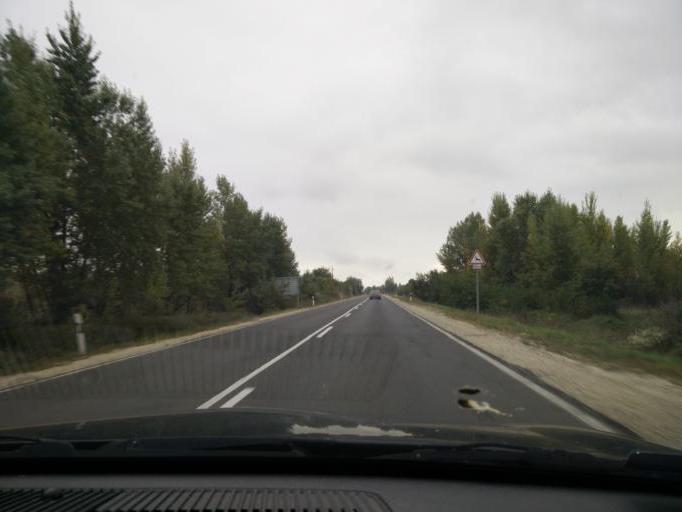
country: HU
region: Komarom-Esztergom
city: Dorog
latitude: 47.7456
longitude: 18.7383
